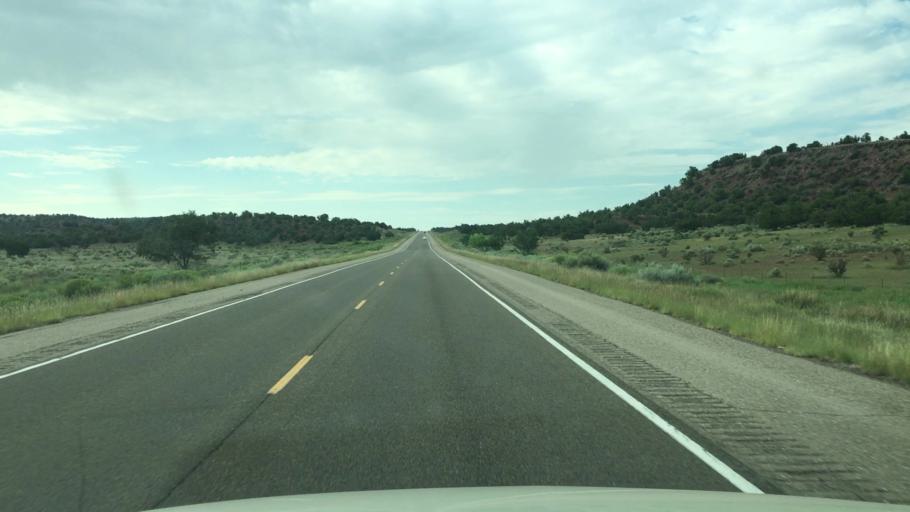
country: US
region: New Mexico
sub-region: Santa Fe County
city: Eldorado at Santa Fe
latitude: 35.2389
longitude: -105.8050
